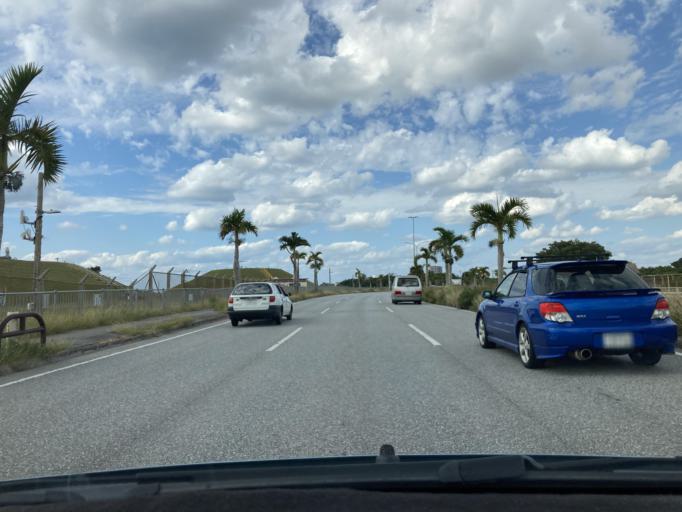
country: JP
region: Okinawa
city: Chatan
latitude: 26.3449
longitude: 127.7477
